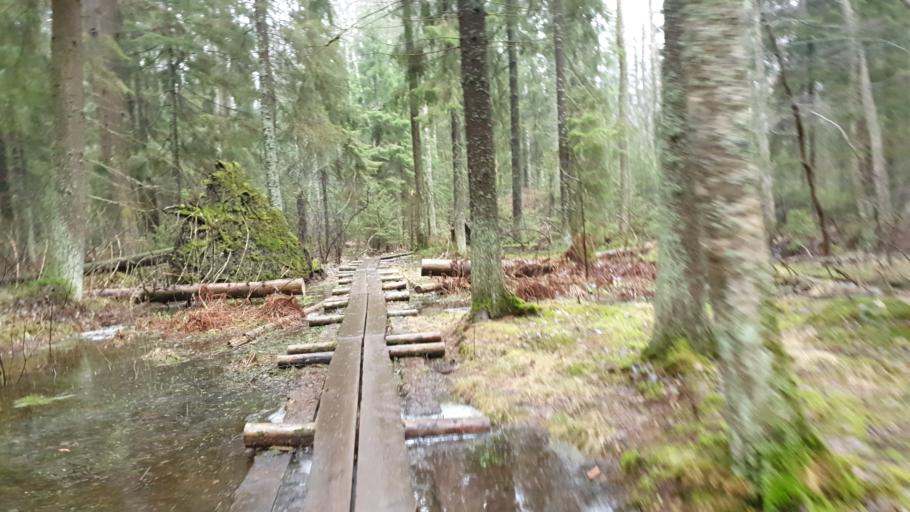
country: FI
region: Uusimaa
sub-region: Helsinki
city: Helsinki
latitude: 60.2648
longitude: 24.9203
